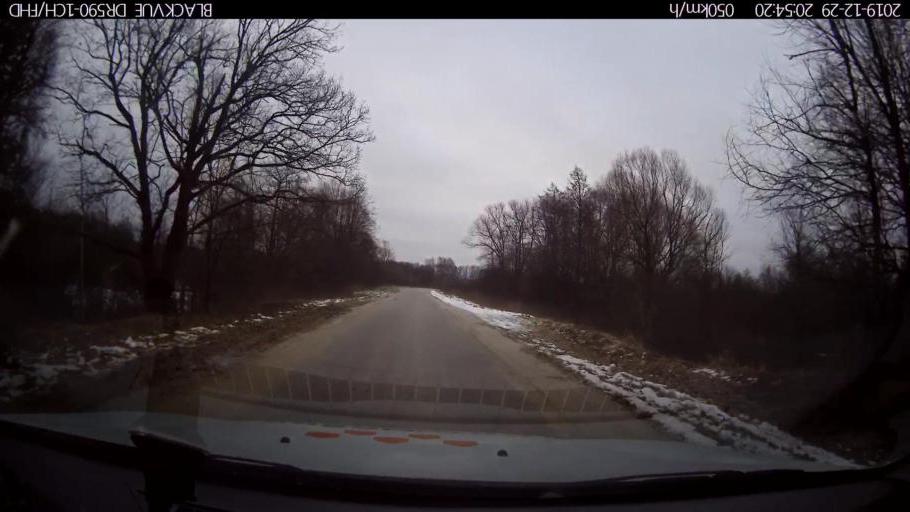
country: RU
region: Nizjnij Novgorod
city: Afonino
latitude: 56.1649
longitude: 43.9887
